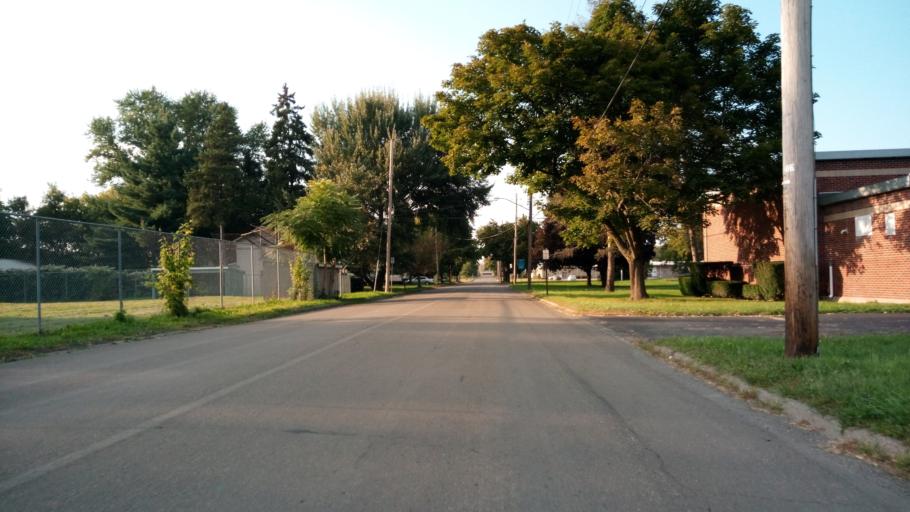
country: US
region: New York
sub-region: Chemung County
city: Elmira
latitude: 42.1113
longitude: -76.8035
